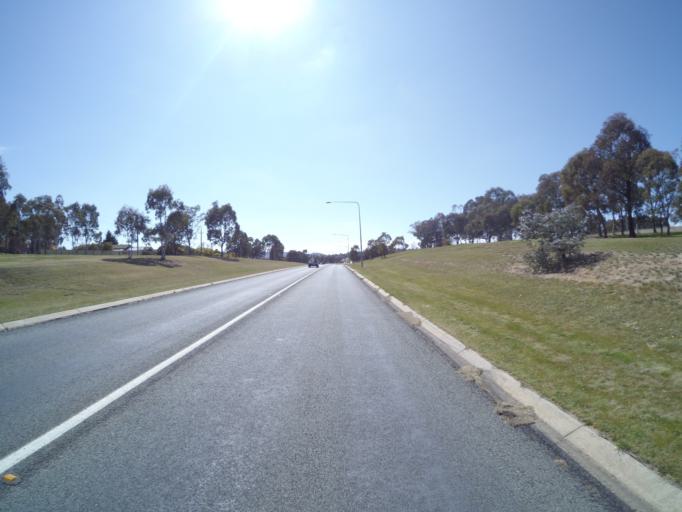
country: AU
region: Australian Capital Territory
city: Macarthur
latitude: -35.4406
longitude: 149.0877
